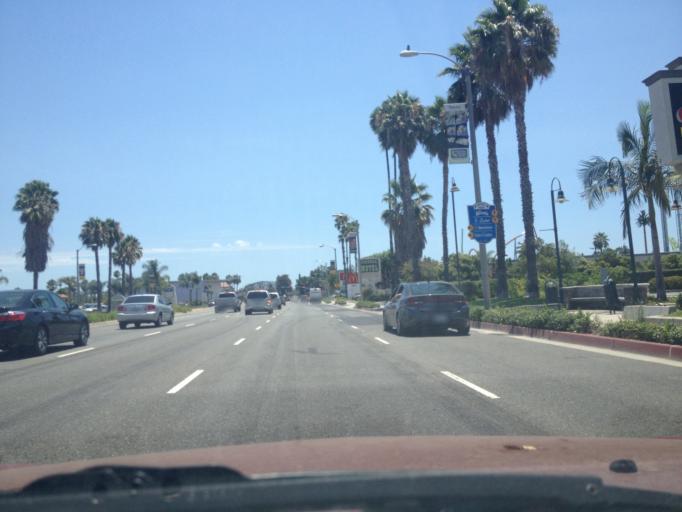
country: US
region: California
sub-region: Orange County
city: Buena Park
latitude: 33.8494
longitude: -117.9981
